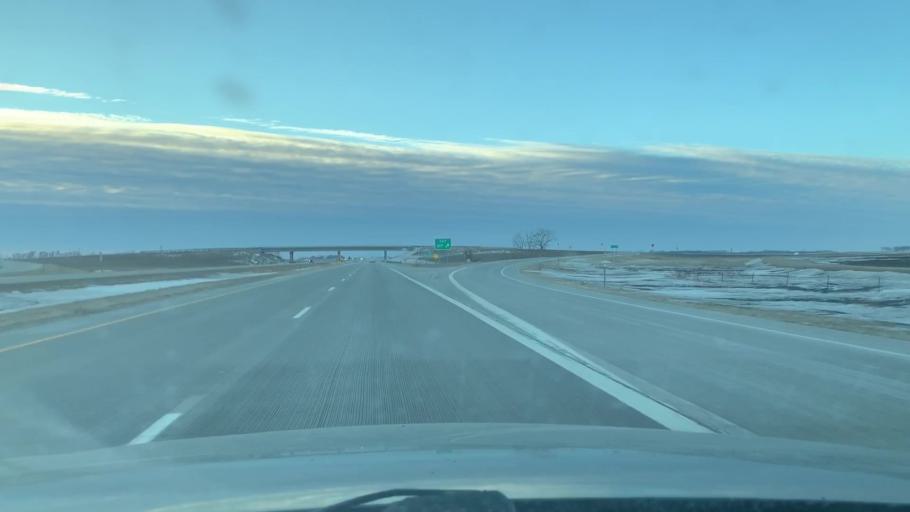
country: US
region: North Dakota
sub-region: Cass County
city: Casselton
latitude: 46.8758
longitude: -97.4885
